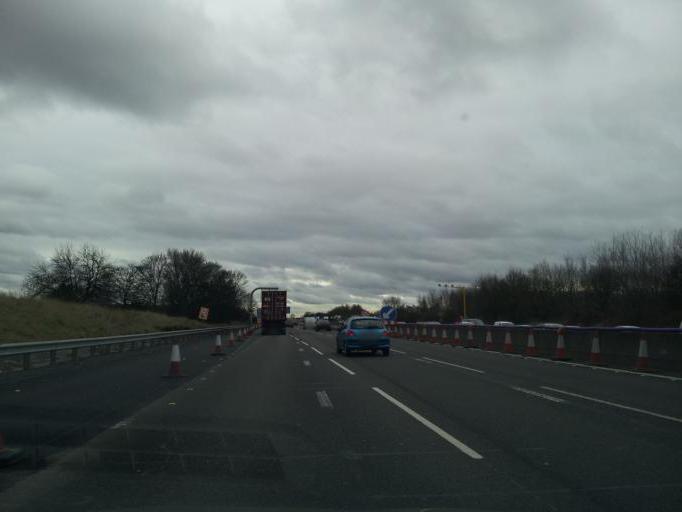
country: GB
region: England
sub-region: Staffordshire
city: Penkridge
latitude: 52.7153
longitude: -2.1016
